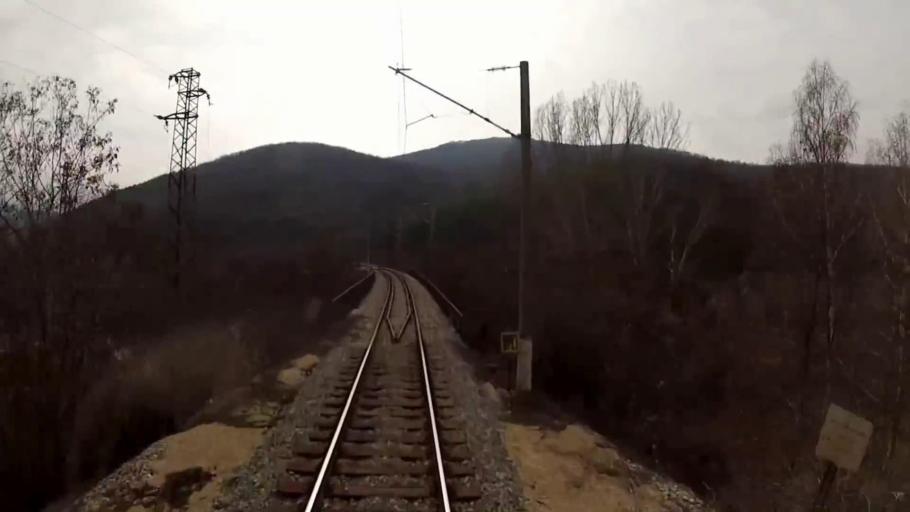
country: BG
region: Sofiya
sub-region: Obshtina Gorna Malina
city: Gorna Malina
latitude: 42.6896
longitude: 23.8035
